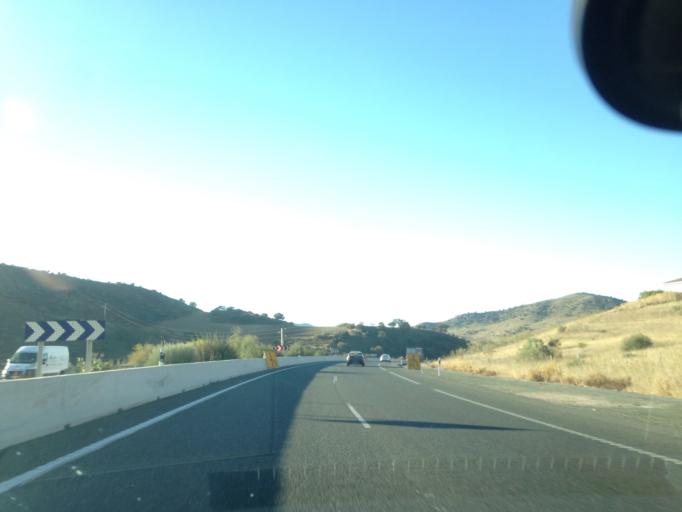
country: ES
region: Andalusia
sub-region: Provincia de Malaga
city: Casabermeja
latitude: 36.9381
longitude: -4.4393
